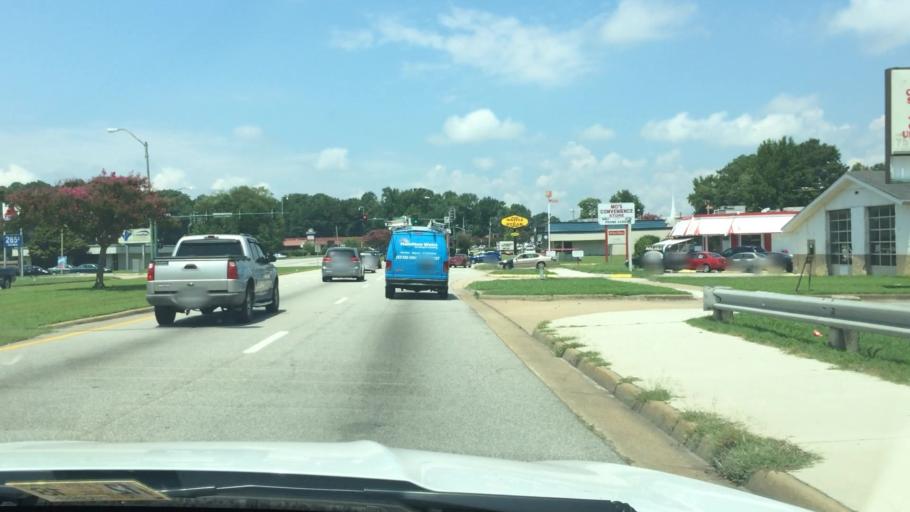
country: US
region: Virginia
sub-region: York County
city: Yorktown
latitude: 37.1321
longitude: -76.5413
